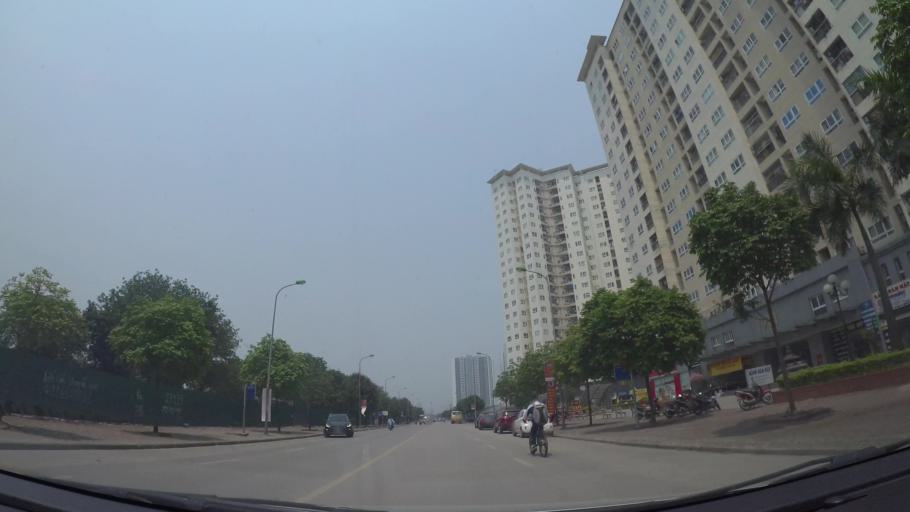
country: VN
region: Ha Noi
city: Thanh Xuan
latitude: 20.9948
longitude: 105.7783
